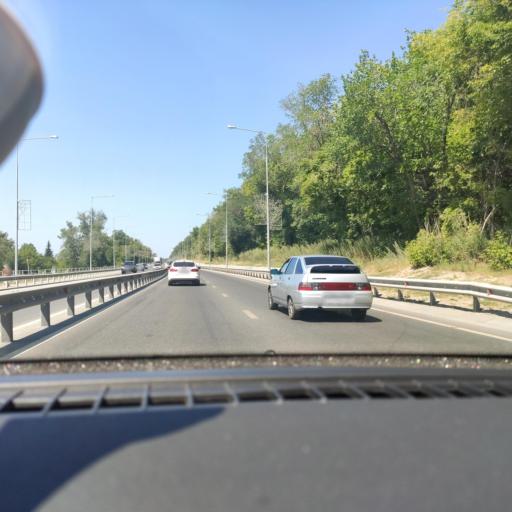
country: RU
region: Samara
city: Volzhskiy
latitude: 53.3871
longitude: 50.1619
